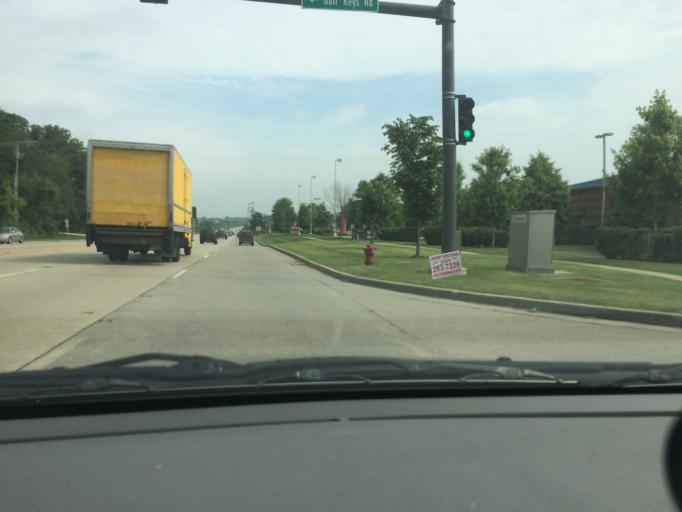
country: US
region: Illinois
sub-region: Cook County
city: Streamwood
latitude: 42.0162
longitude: -88.2030
